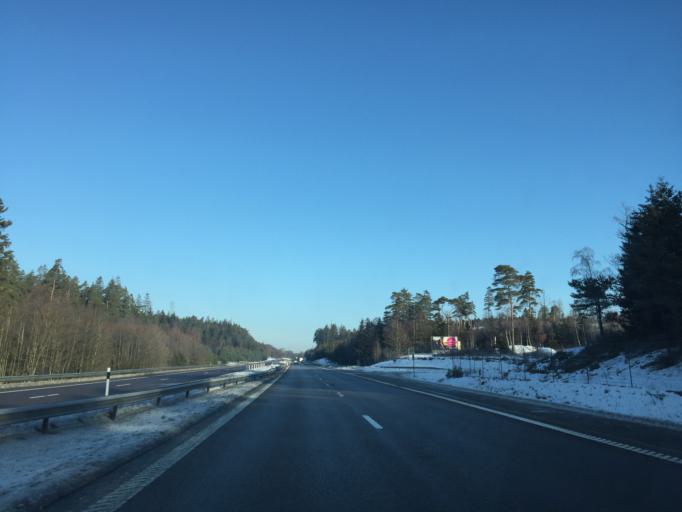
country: SE
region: Vaestra Goetaland
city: Svanesund
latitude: 58.1355
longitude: 11.8859
